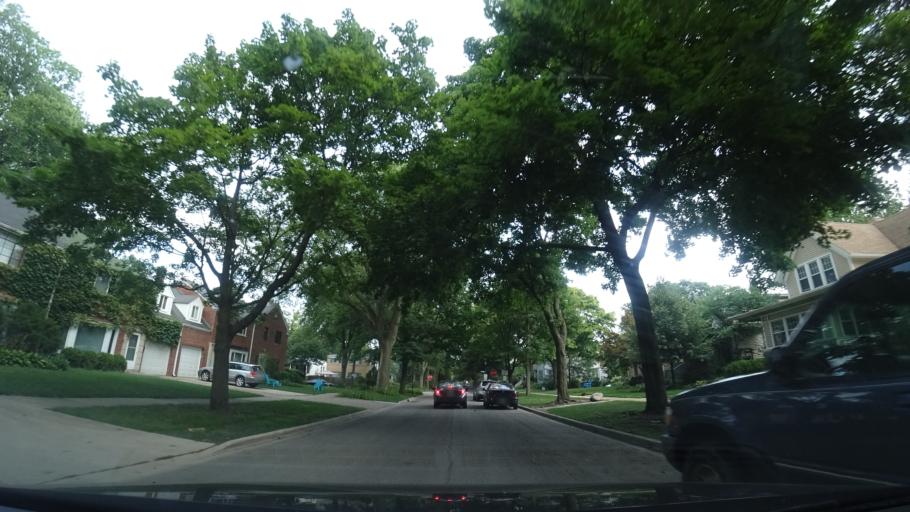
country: US
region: Illinois
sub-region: Cook County
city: Evanston
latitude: 42.0592
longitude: -87.7012
